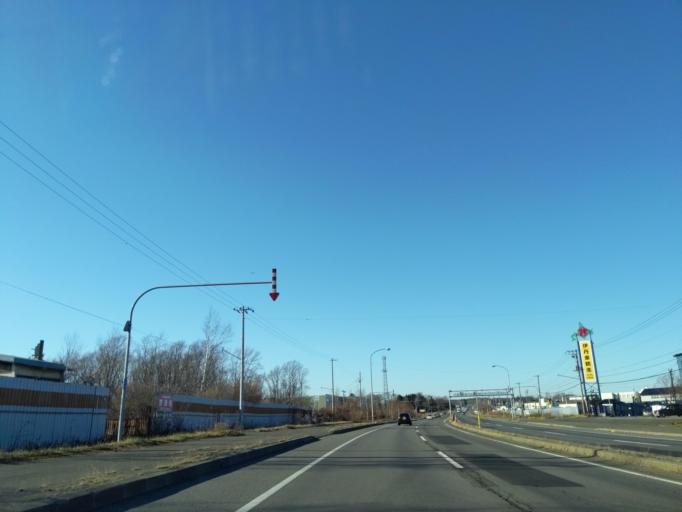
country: JP
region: Hokkaido
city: Kitahiroshima
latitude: 42.9363
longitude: 141.5138
